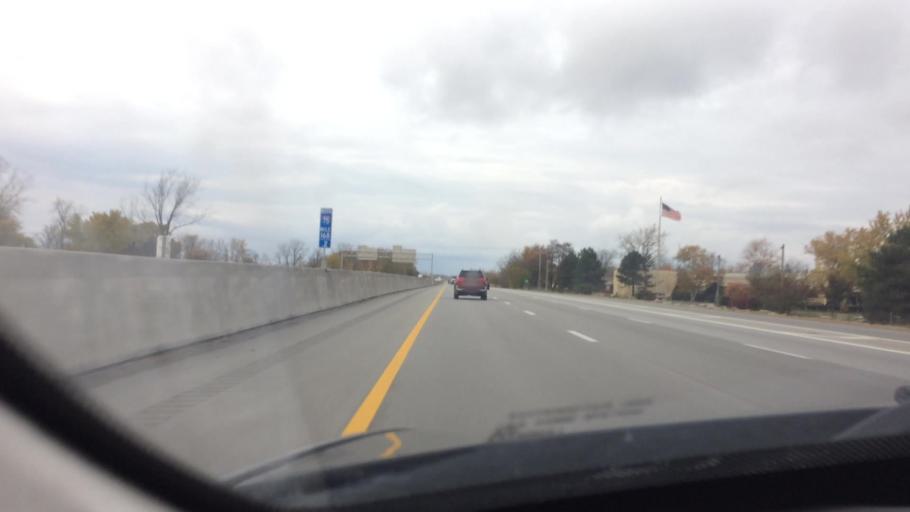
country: US
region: Ohio
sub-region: Wood County
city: North Baltimore
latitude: 41.1876
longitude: -83.6495
